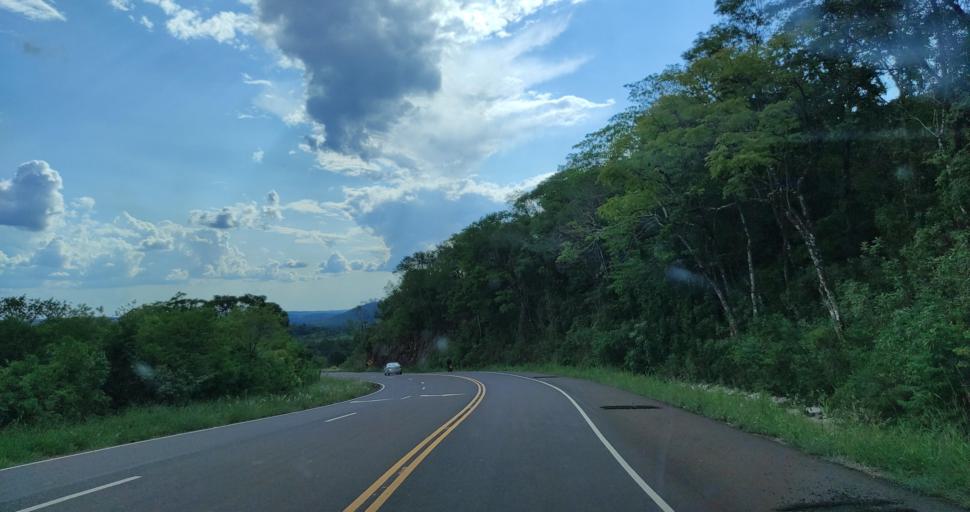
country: AR
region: Misiones
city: Bernardo de Irigoyen
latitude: -26.3040
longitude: -53.8153
